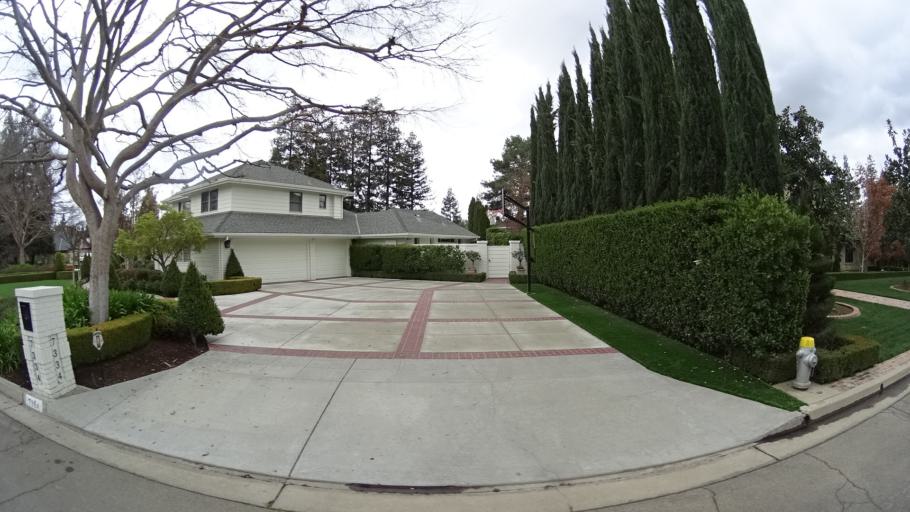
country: US
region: California
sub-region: Fresno County
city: Fresno
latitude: 36.8431
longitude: -119.8337
